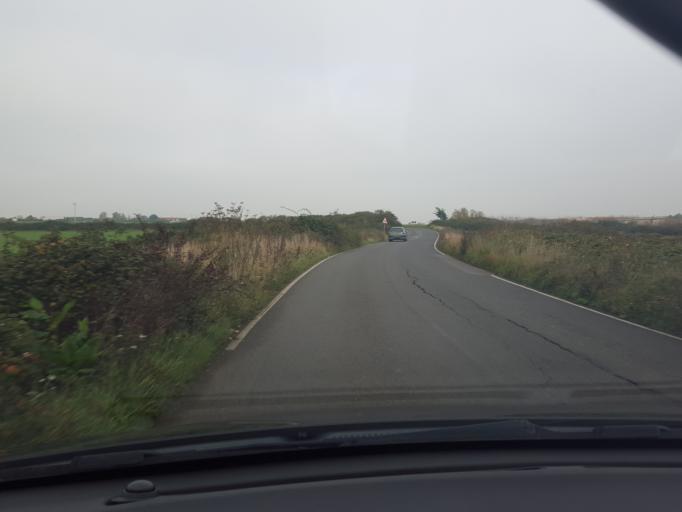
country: GB
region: England
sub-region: Essex
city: Saint Osyth
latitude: 51.7805
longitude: 1.0883
